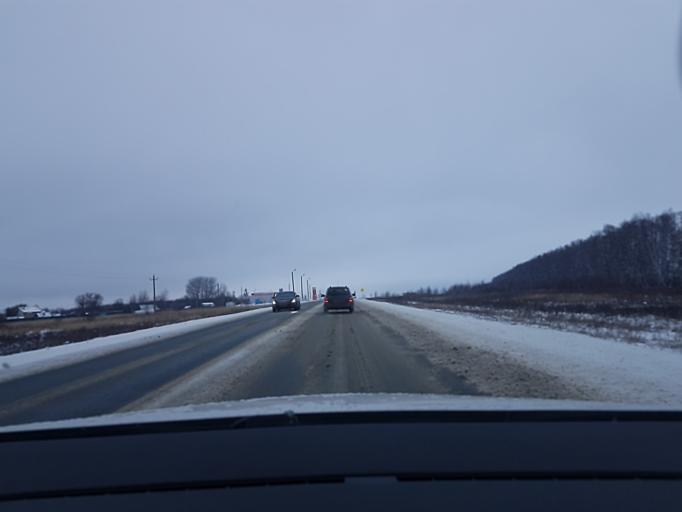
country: RU
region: Moskovskaya
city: Uzunovo
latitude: 54.5799
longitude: 38.4430
